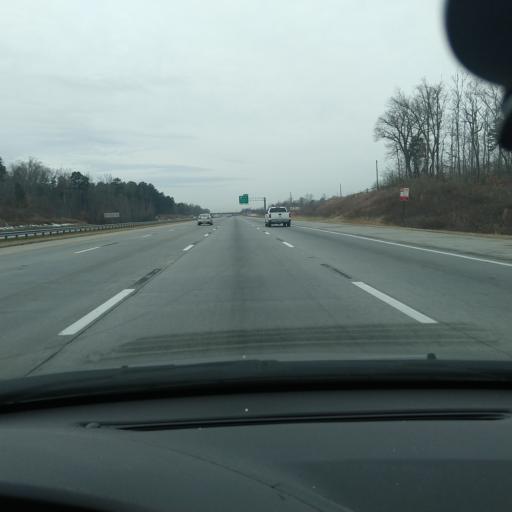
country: US
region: North Carolina
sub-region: Rowan County
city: East Spencer
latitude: 35.6680
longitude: -80.4384
